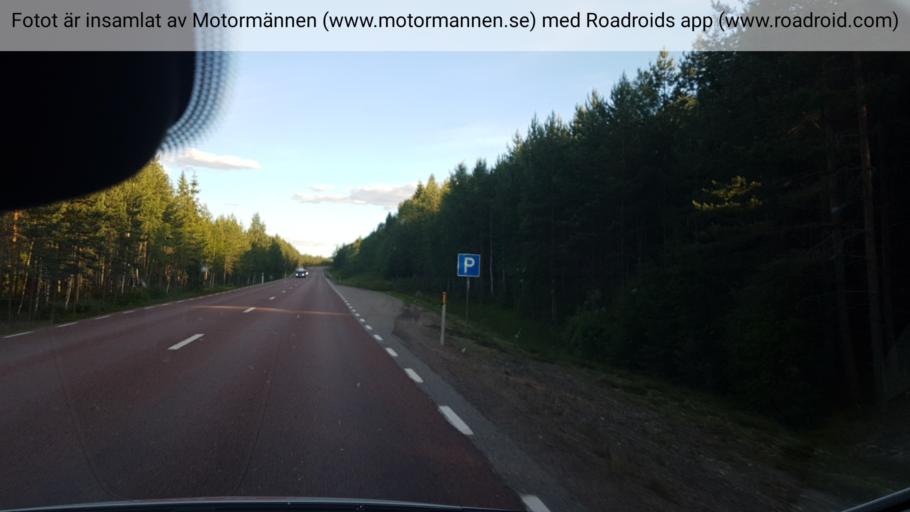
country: SE
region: Vaermland
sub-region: Hagfors Kommun
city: Ekshaerad
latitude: 60.4043
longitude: 13.2596
